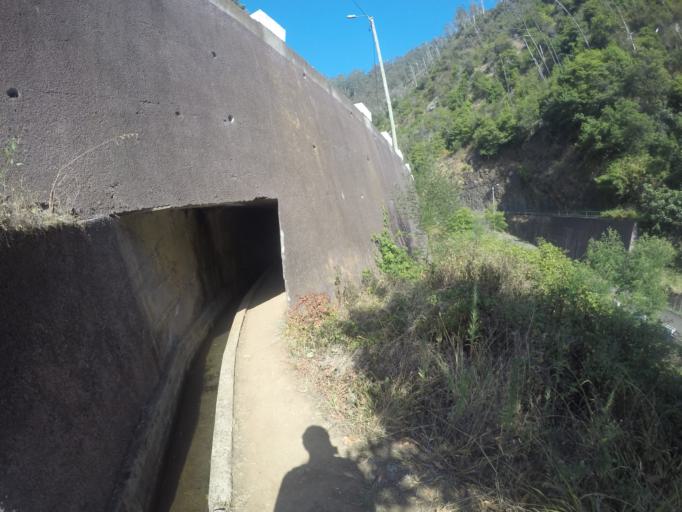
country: PT
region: Madeira
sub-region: Santana
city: Santana
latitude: 32.7590
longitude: -16.8318
